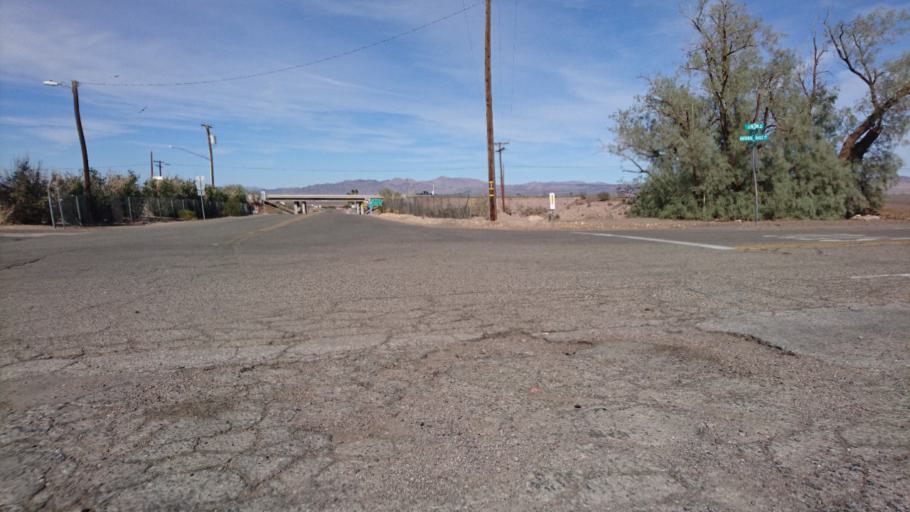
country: US
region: California
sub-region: San Bernardino County
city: Twentynine Palms
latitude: 34.7237
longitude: -116.1631
